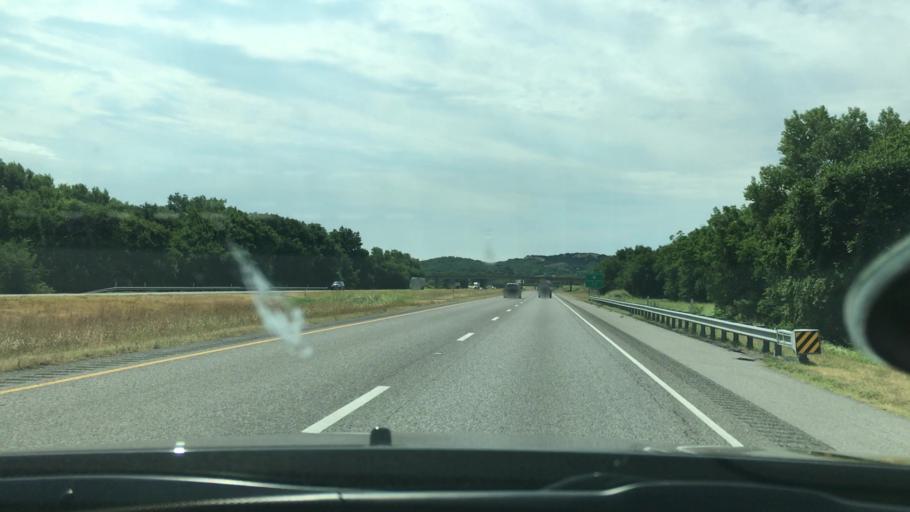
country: US
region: Oklahoma
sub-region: Murray County
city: Davis
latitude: 34.4582
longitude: -97.1429
